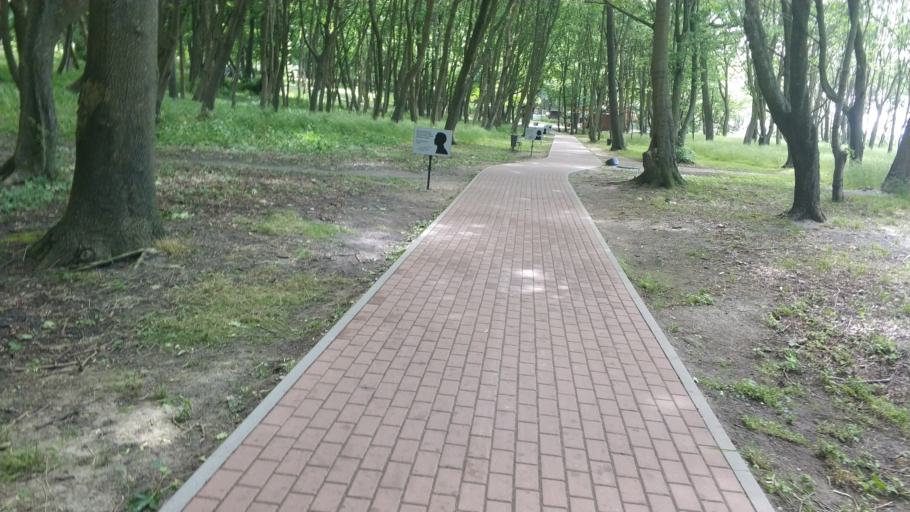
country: RU
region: Kaliningrad
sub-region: Gorod Kaliningrad
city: Yantarnyy
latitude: 54.8682
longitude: 19.9345
